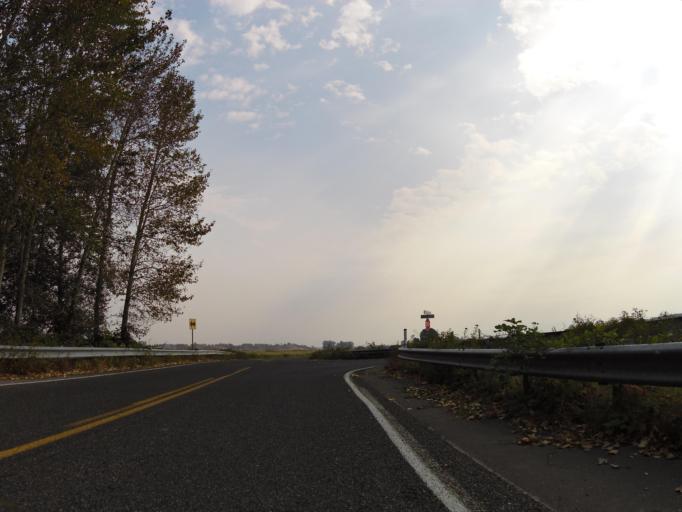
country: US
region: Washington
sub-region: Whatcom County
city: Ferndale
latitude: 48.8085
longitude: -122.6504
